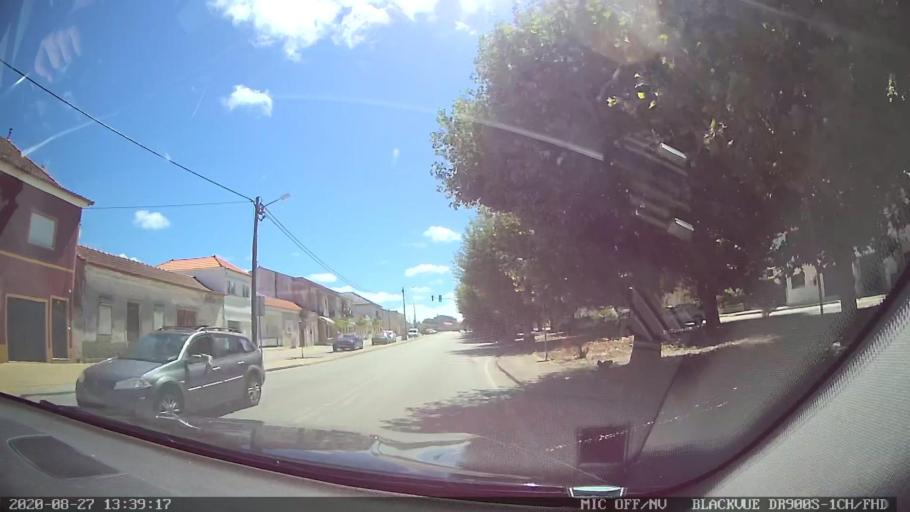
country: PT
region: Coimbra
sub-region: Mira
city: Mira
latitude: 40.4424
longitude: -8.7289
